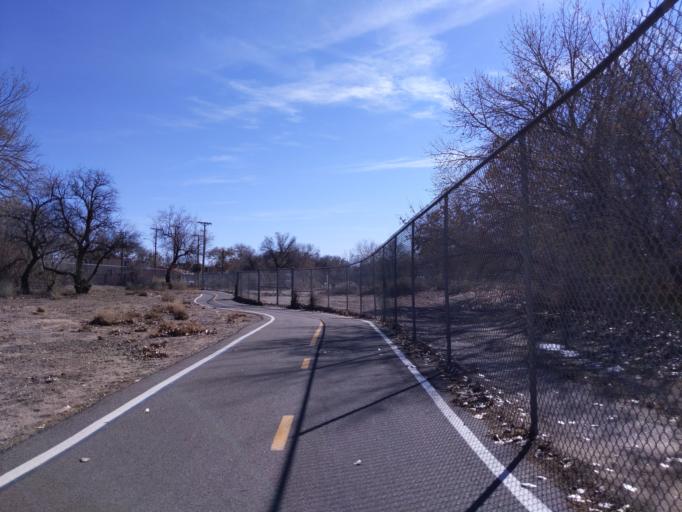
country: US
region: New Mexico
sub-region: Bernalillo County
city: Albuquerque
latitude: 35.1004
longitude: -106.6879
